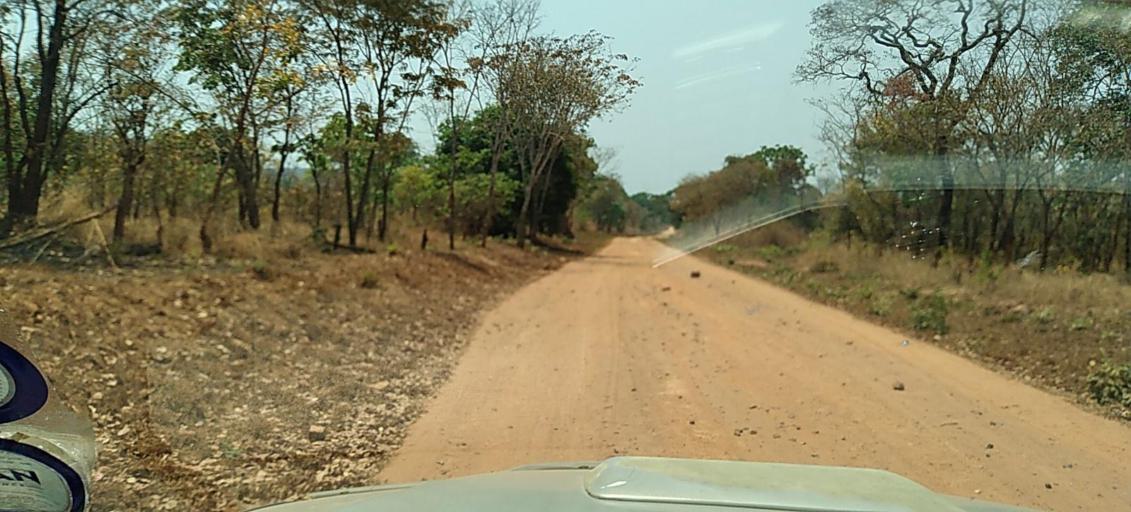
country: ZM
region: North-Western
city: Kasempa
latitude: -13.5508
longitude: 26.0176
